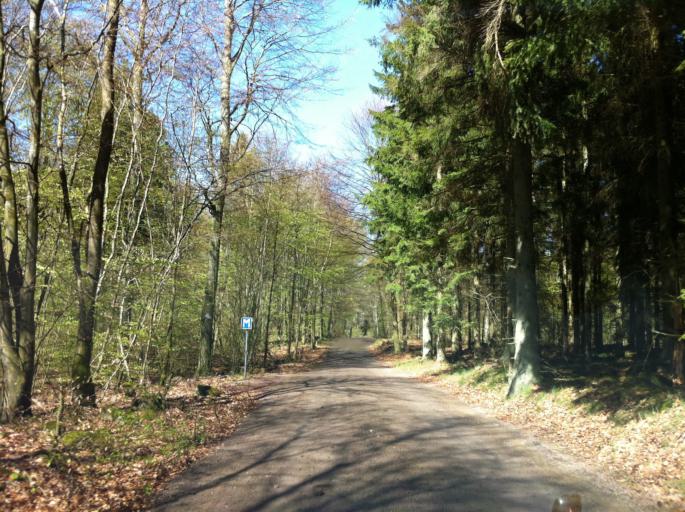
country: SE
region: Skane
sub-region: Horby Kommun
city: Hoerby
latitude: 55.8850
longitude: 13.6461
